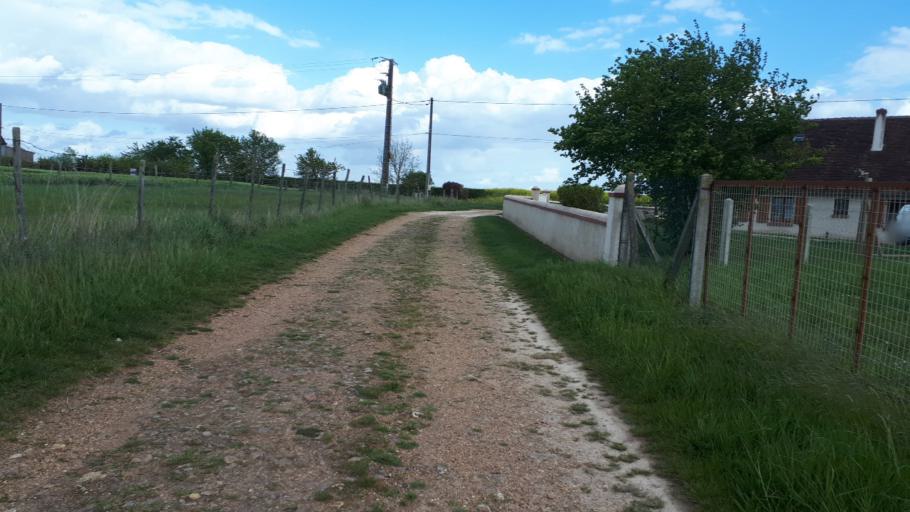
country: FR
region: Centre
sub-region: Departement du Loir-et-Cher
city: Aze
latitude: 47.8357
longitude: 1.0018
